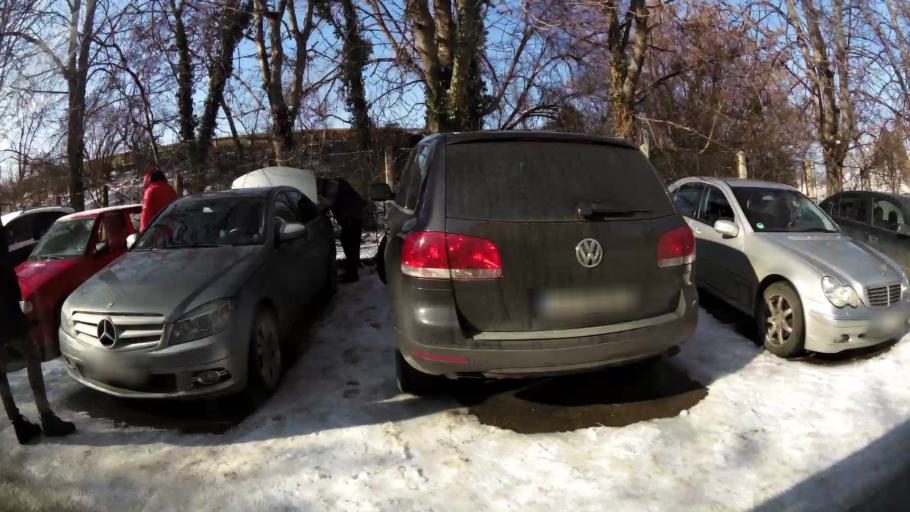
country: BG
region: Sofia-Capital
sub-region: Stolichna Obshtina
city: Sofia
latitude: 42.6775
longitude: 23.3053
